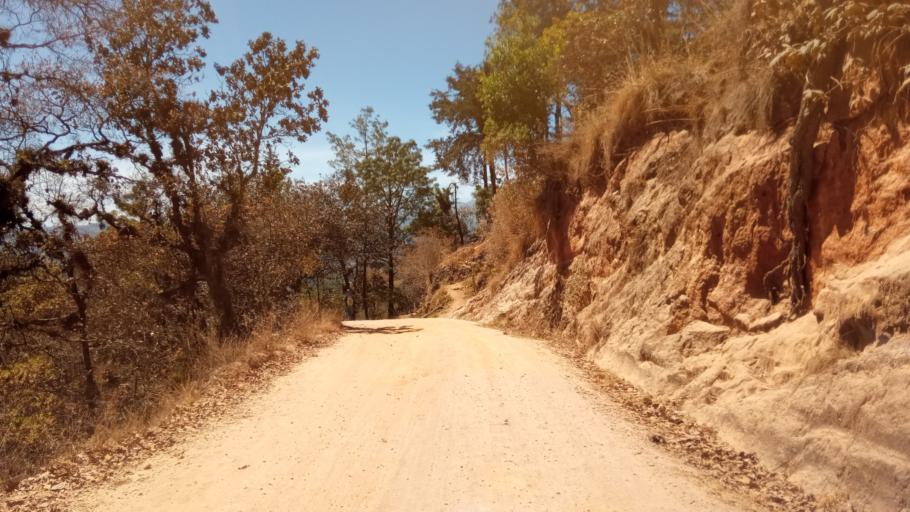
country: GT
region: San Marcos
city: Tejutla
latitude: 15.1374
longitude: -91.7931
